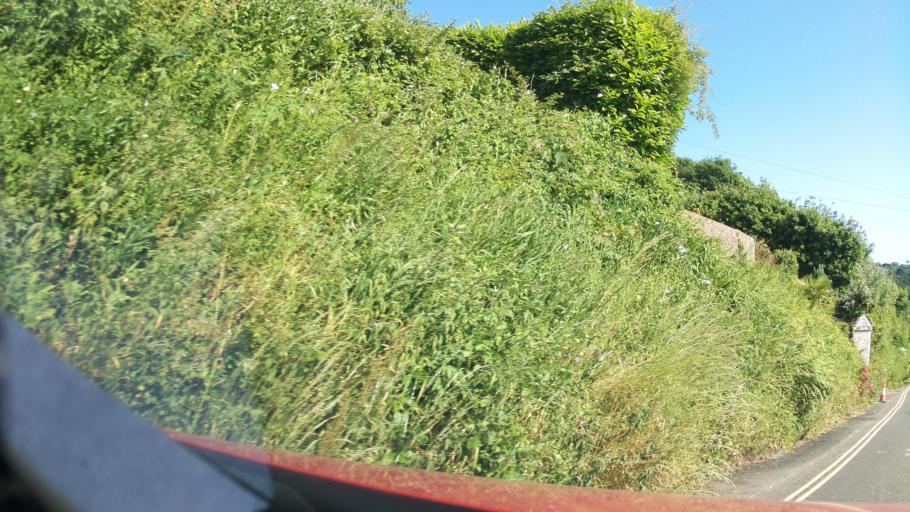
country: GB
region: England
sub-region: Devon
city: Dartmouth
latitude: 50.3621
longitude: -3.5745
